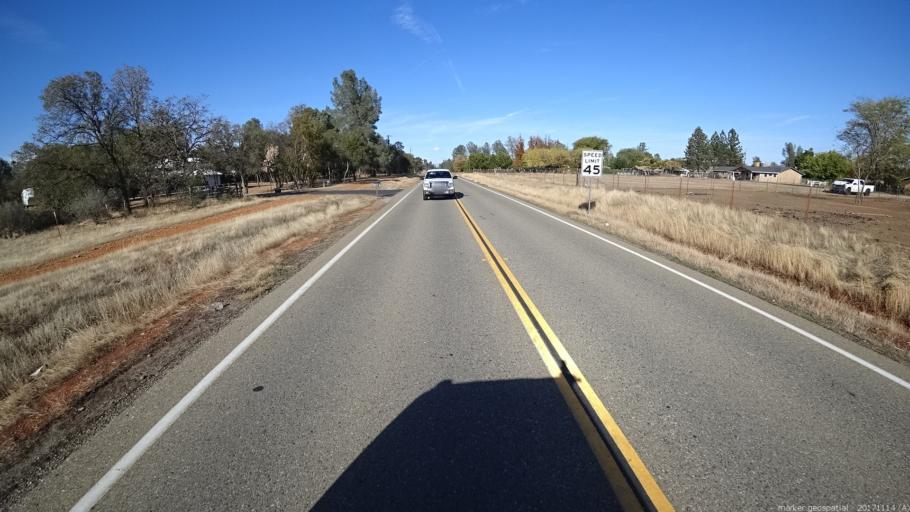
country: US
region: California
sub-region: Shasta County
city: Anderson
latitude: 40.4228
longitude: -122.4070
